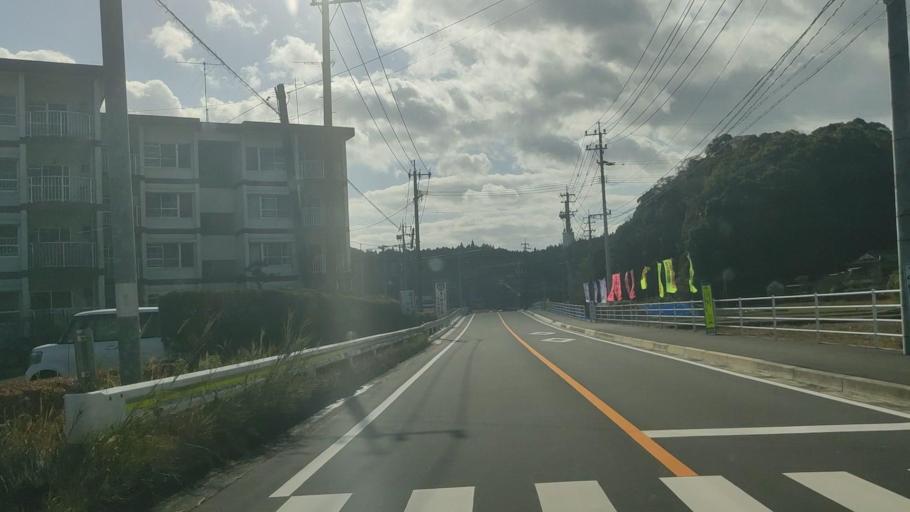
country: JP
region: Kagoshima
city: Okuchi-shinohara
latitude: 31.9425
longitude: 130.7102
